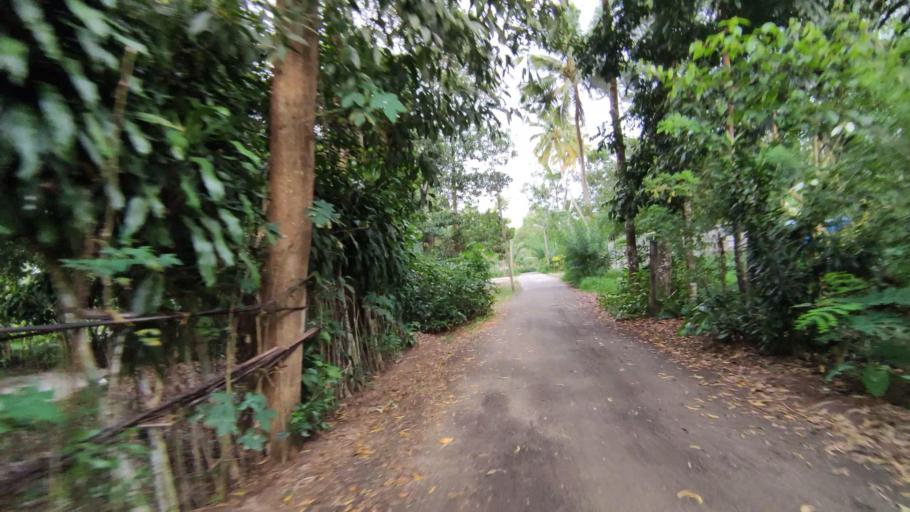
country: IN
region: Kerala
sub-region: Alappuzha
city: Shertallai
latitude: 9.6112
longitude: 76.3491
